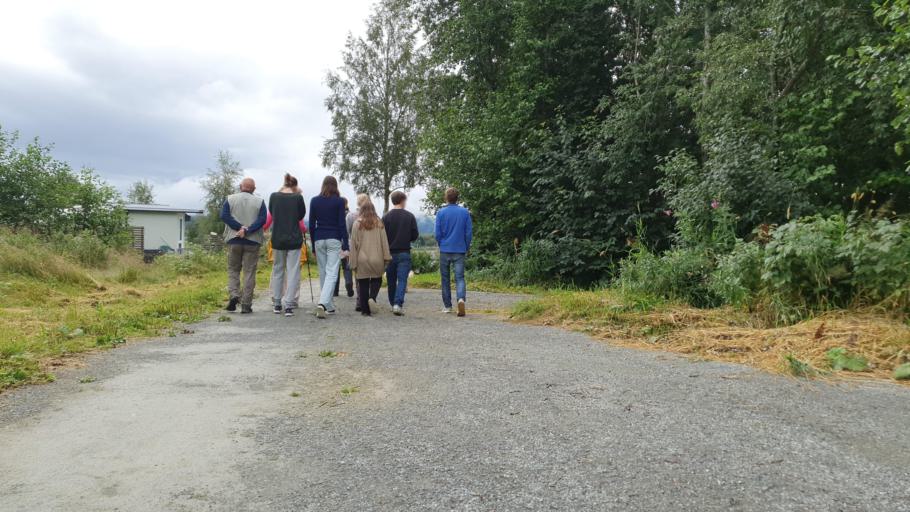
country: NO
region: Sor-Trondelag
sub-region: Selbu
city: Mebonden
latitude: 63.2302
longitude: 11.0228
